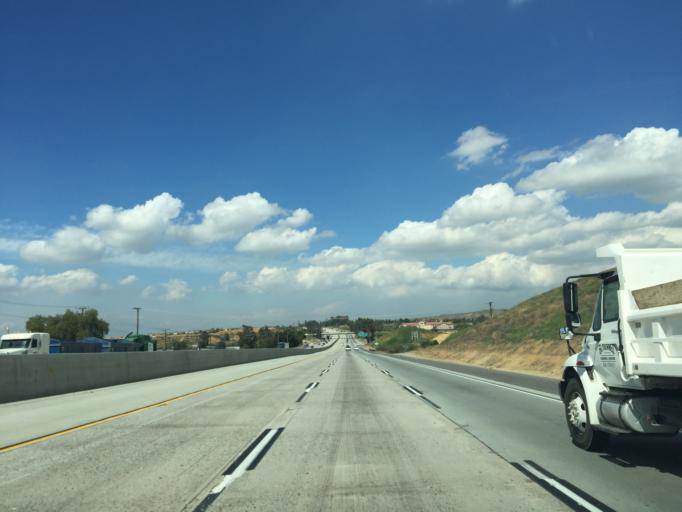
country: US
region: California
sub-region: Riverside County
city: Beaumont
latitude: 33.9391
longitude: -116.9980
